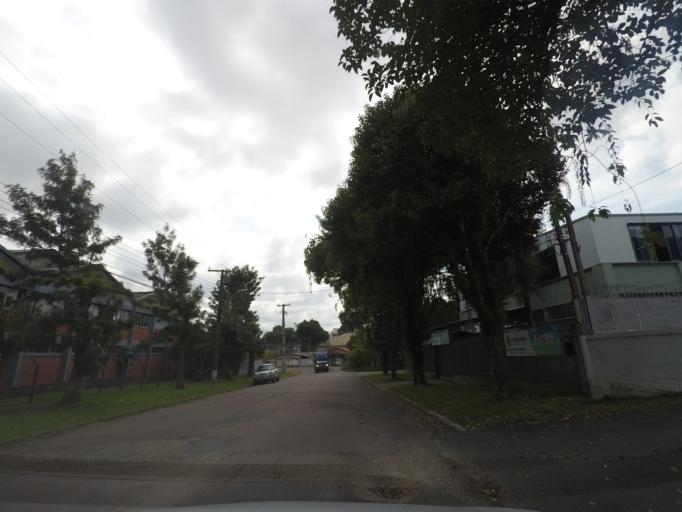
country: BR
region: Parana
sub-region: Curitiba
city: Curitiba
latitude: -25.4927
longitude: -49.3285
